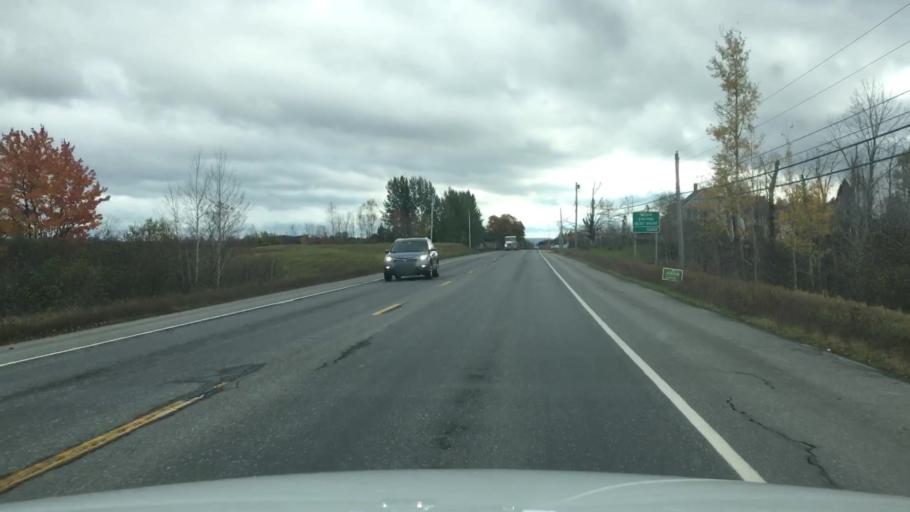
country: US
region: Maine
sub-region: Aroostook County
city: Houlton
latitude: 46.1842
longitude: -67.8412
